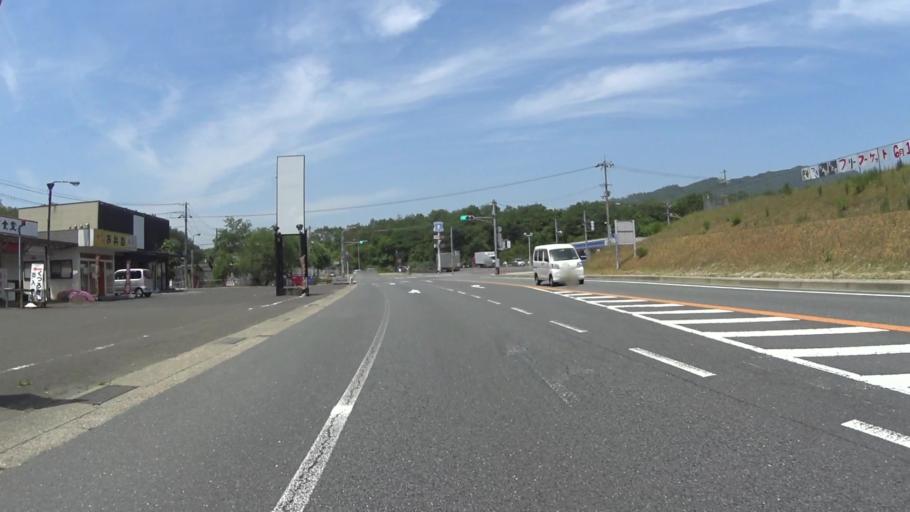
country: JP
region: Kyoto
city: Fukuchiyama
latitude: 35.2727
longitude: 135.1832
